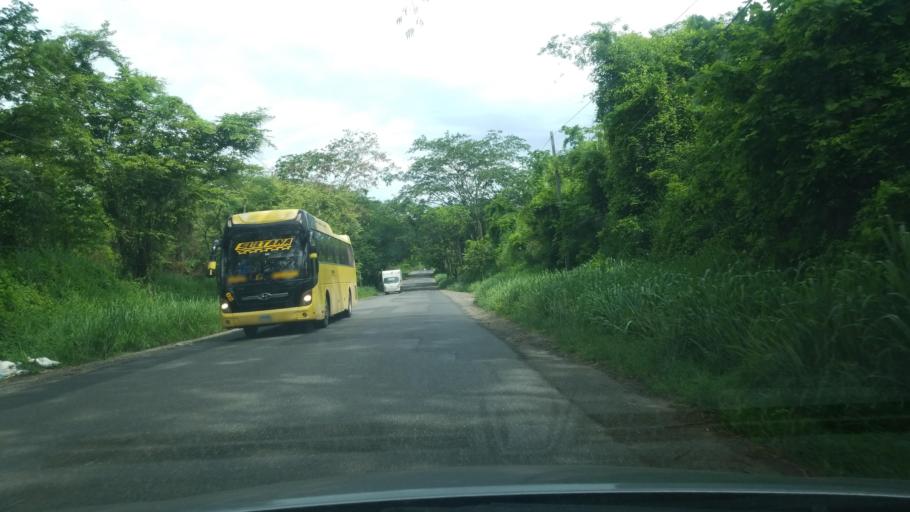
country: HN
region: Santa Barbara
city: Camalote
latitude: 15.3338
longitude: -88.3482
